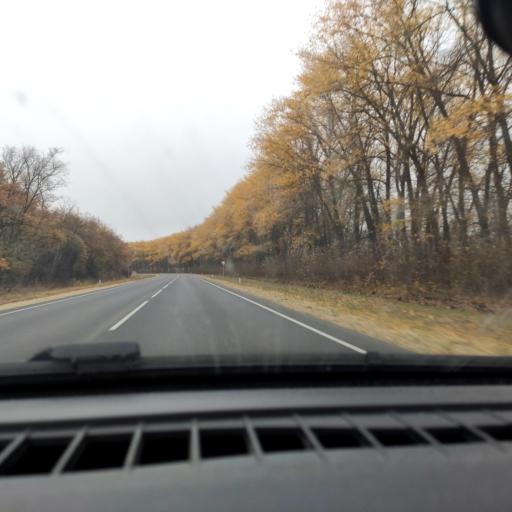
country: RU
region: Voronezj
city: Uryv-Pokrovka
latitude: 51.1869
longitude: 39.0858
